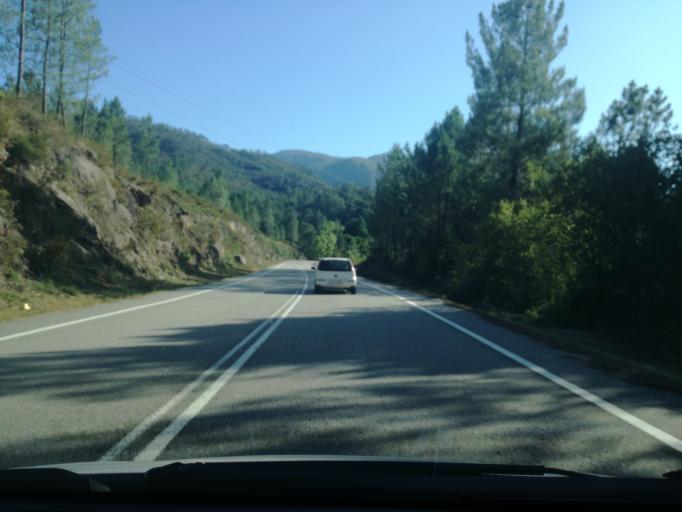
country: ES
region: Galicia
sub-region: Provincia de Ourense
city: Entrimo
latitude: 41.8750
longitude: -8.1670
